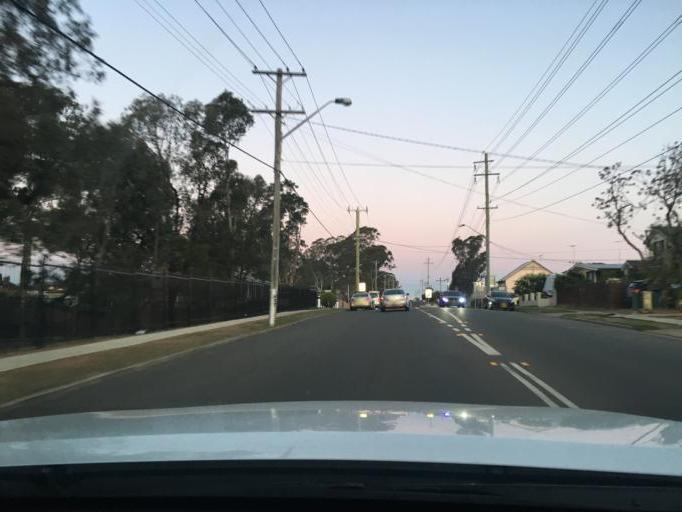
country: AU
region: New South Wales
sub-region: Holroyd
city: Girraween
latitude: -33.8287
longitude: 150.9419
